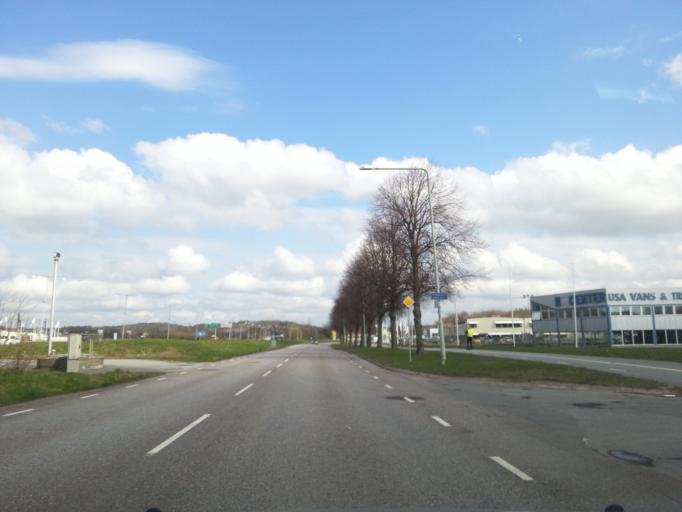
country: SE
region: Vaestra Goetaland
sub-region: Goteborg
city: Hammarkullen
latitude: 57.7817
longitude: 12.0000
